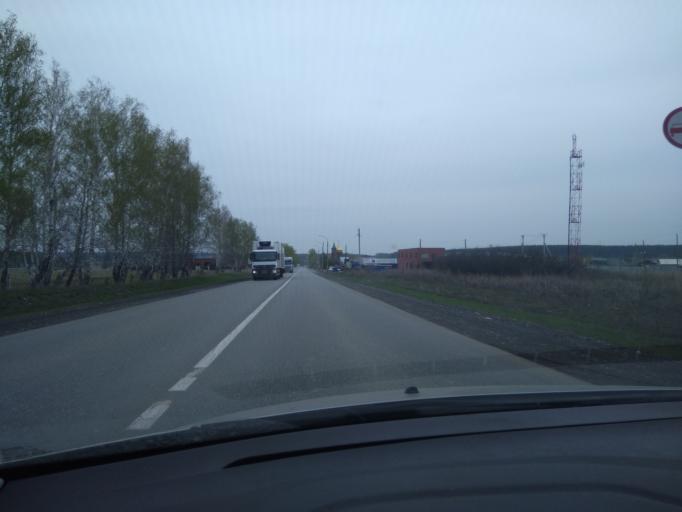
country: RU
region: Sverdlovsk
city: Zarechnyy
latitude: 56.7490
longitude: 61.3116
